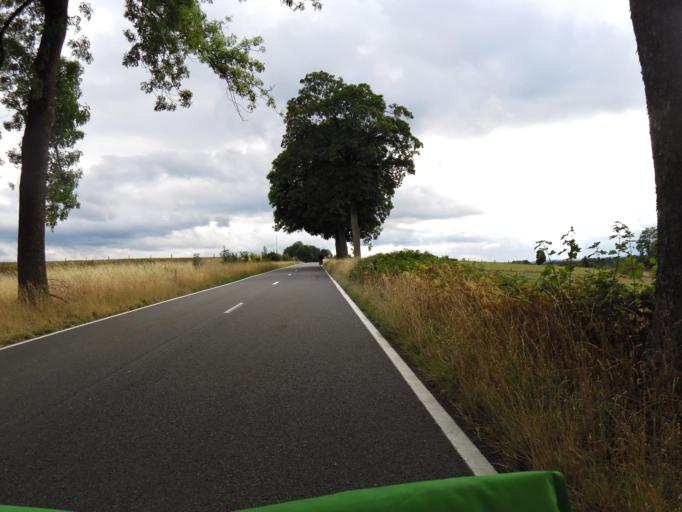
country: BE
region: Wallonia
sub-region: Province de Namur
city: Bievre
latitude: 49.9157
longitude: 4.9979
